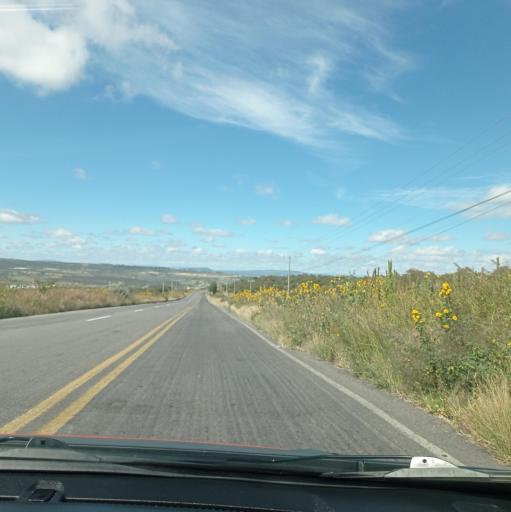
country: MX
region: Jalisco
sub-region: San Julian
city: Colonia Veintitres de Mayo
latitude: 21.0088
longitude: -102.2627
